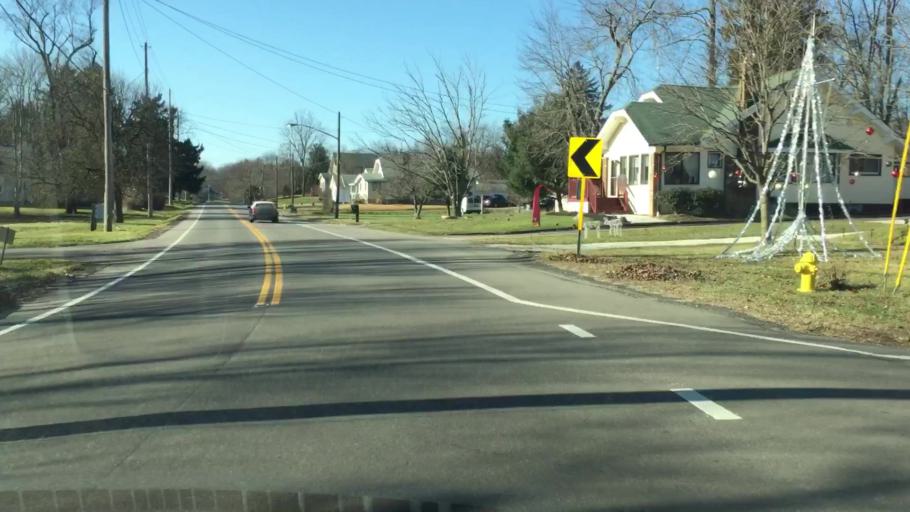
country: US
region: Ohio
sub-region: Summit County
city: Fairlawn
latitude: 41.0888
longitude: -81.6042
